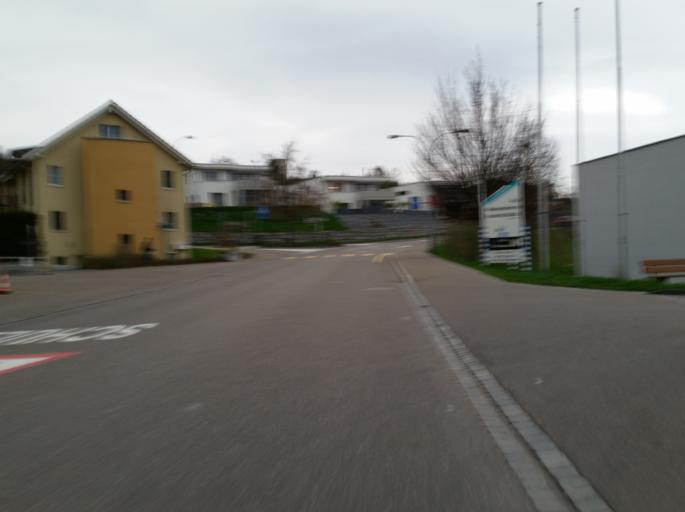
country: CH
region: Appenzell Ausserrhoden
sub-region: Bezirk Vorderland
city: Heiden
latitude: 47.4779
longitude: 9.5429
